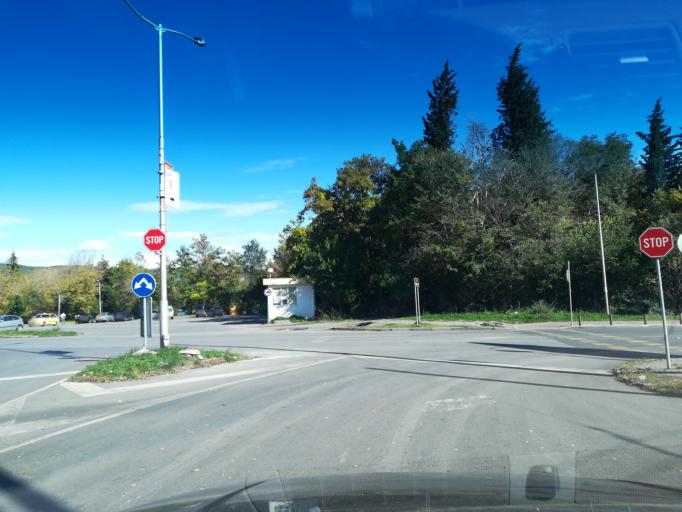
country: BG
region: Stara Zagora
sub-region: Obshtina Stara Zagora
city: Stara Zagora
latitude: 42.4429
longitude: 25.6344
